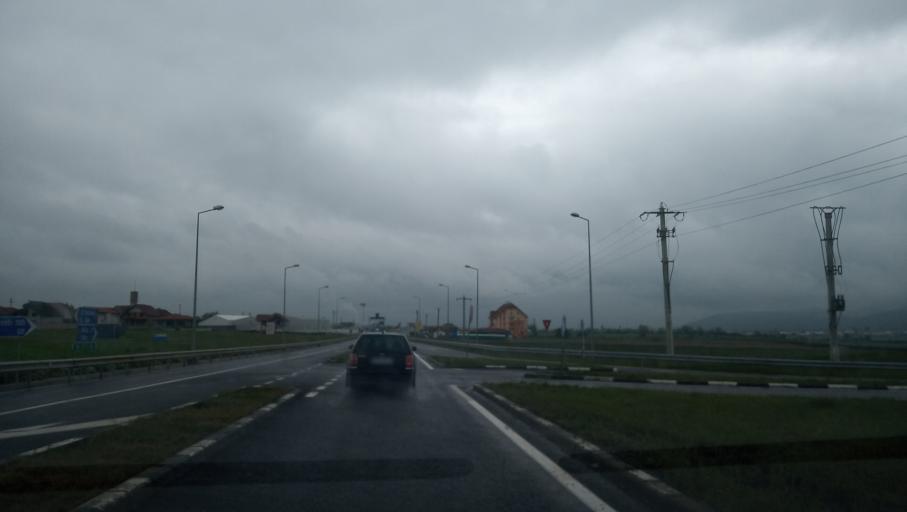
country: RO
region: Alba
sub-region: Municipiul Sebes
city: Sebes
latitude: 45.9447
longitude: 23.5901
